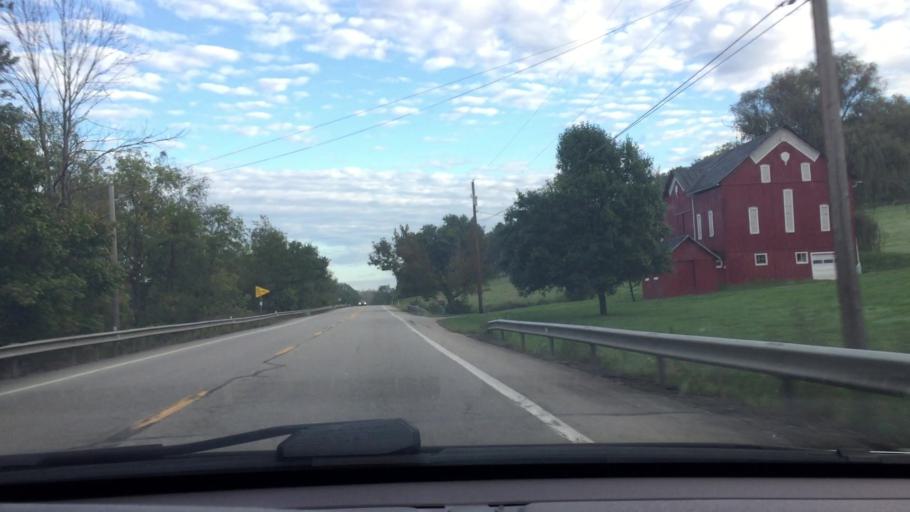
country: US
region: Pennsylvania
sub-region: Washington County
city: McGovern
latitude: 40.1661
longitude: -80.1338
